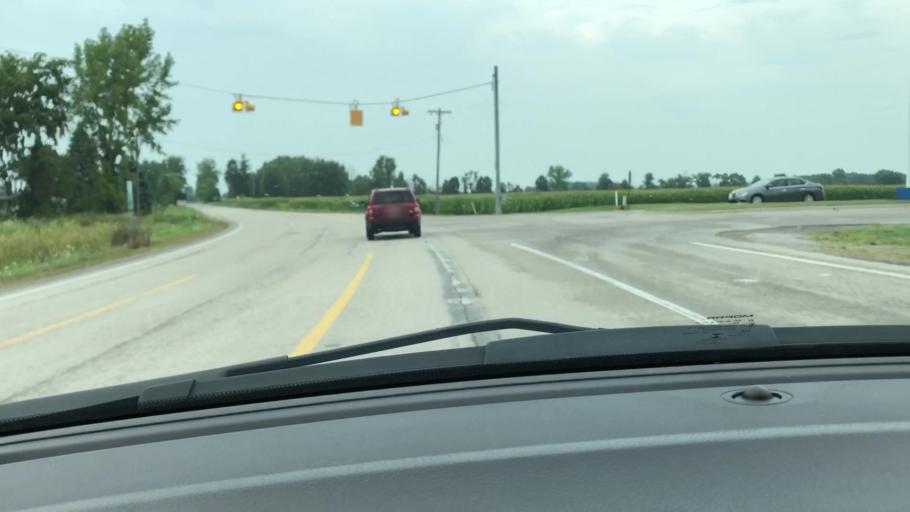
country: US
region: Michigan
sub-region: Saginaw County
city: Freeland
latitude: 43.5421
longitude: -84.0905
